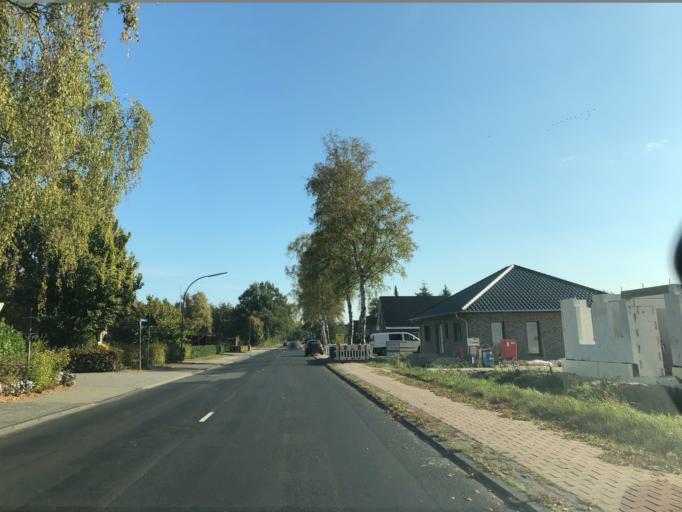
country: DE
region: Lower Saxony
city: Lehe
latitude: 53.0501
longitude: 7.3385
